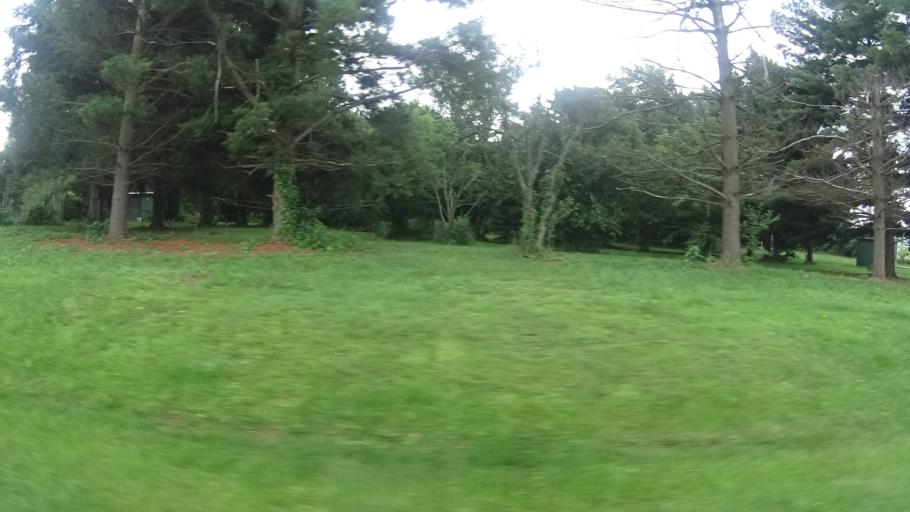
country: US
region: Ohio
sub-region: Huron County
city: Wakeman
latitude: 41.2969
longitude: -82.4926
